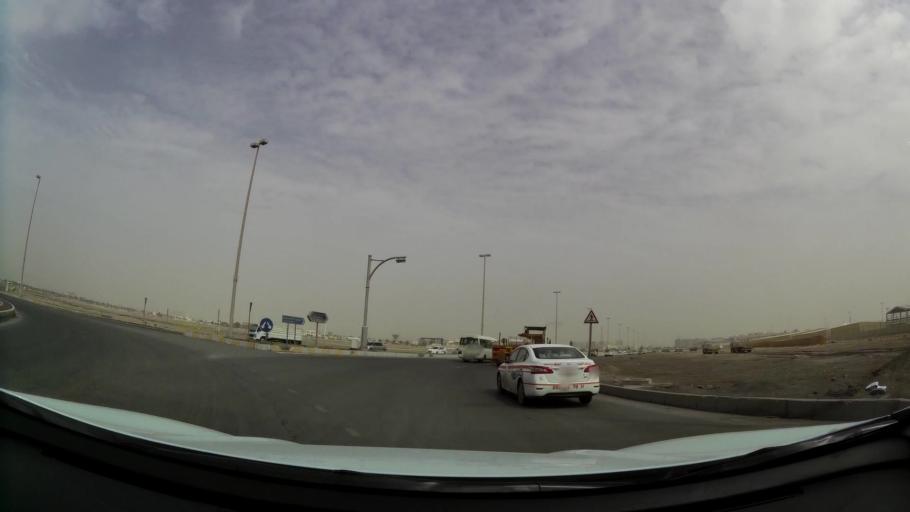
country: AE
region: Abu Dhabi
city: Abu Dhabi
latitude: 24.3369
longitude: 54.5128
